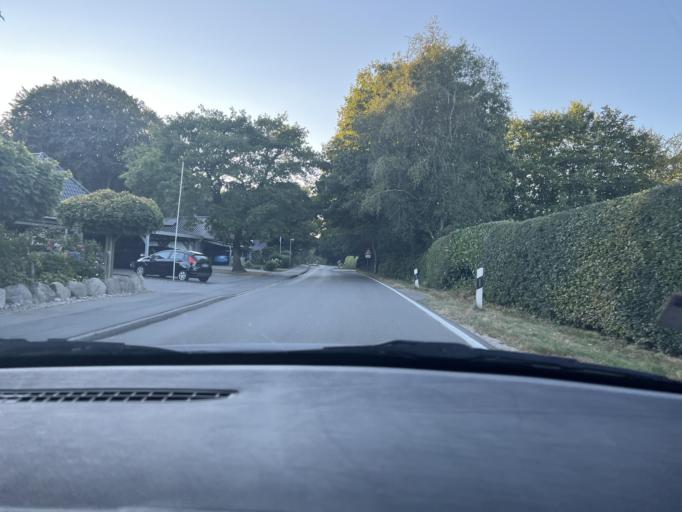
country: DE
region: Schleswig-Holstein
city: Suderheistedt
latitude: 54.2235
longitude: 9.1185
